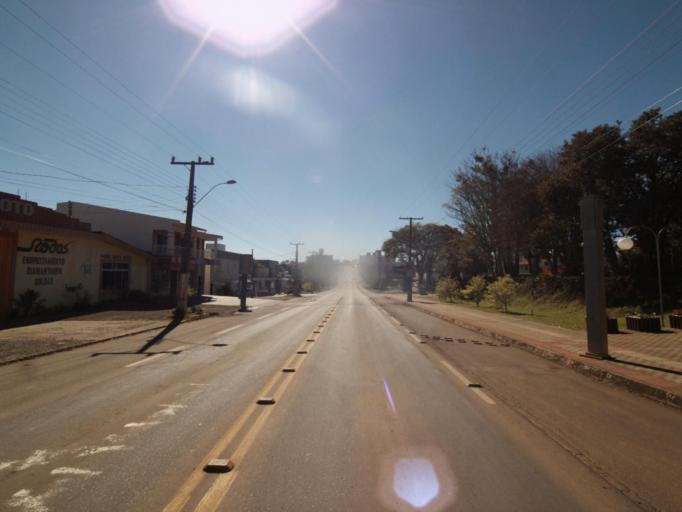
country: AR
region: Misiones
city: Bernardo de Irigoyen
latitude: -26.7380
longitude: -53.5194
